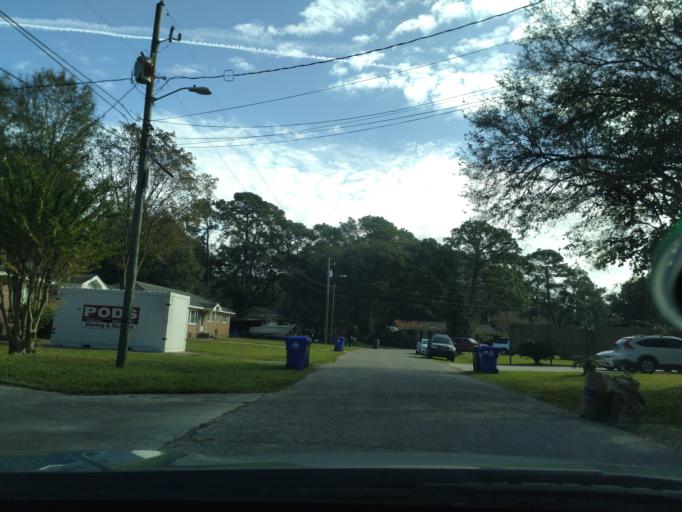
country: US
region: South Carolina
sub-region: Charleston County
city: North Charleston
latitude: 32.8064
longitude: -80.0067
